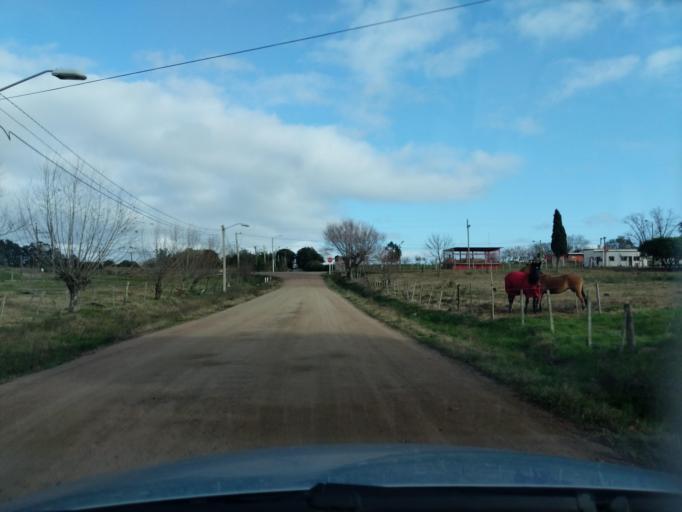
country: UY
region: Florida
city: Florida
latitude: -34.0801
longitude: -56.2107
